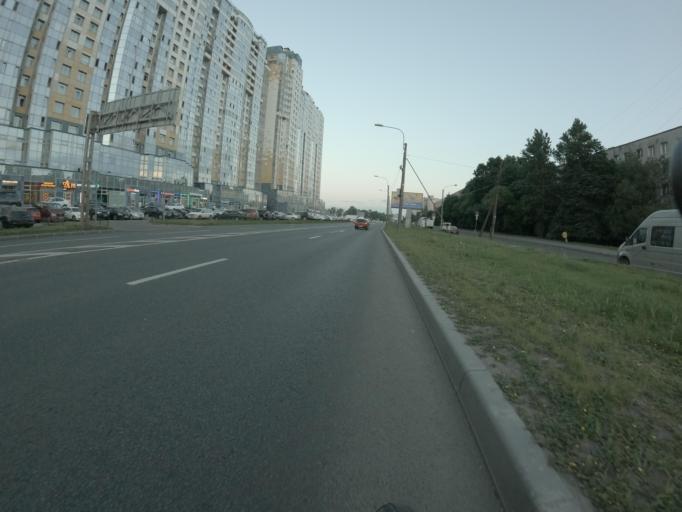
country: RU
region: St.-Petersburg
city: Avtovo
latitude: 59.8510
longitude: 30.2803
